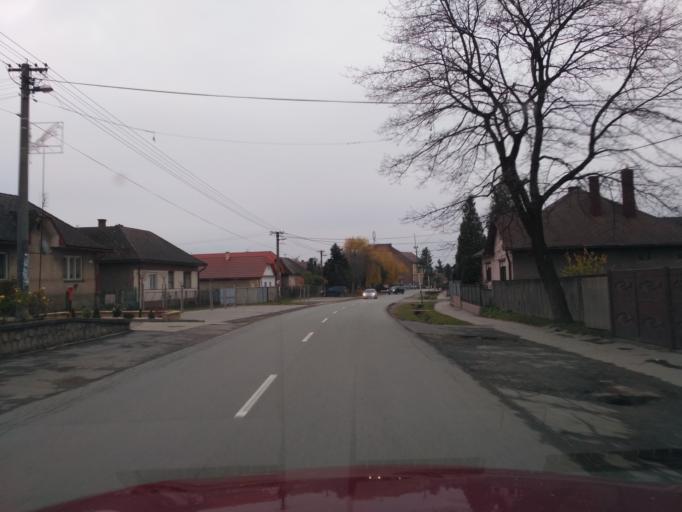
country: SK
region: Kosicky
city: Kosice
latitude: 48.5956
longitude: 21.1689
